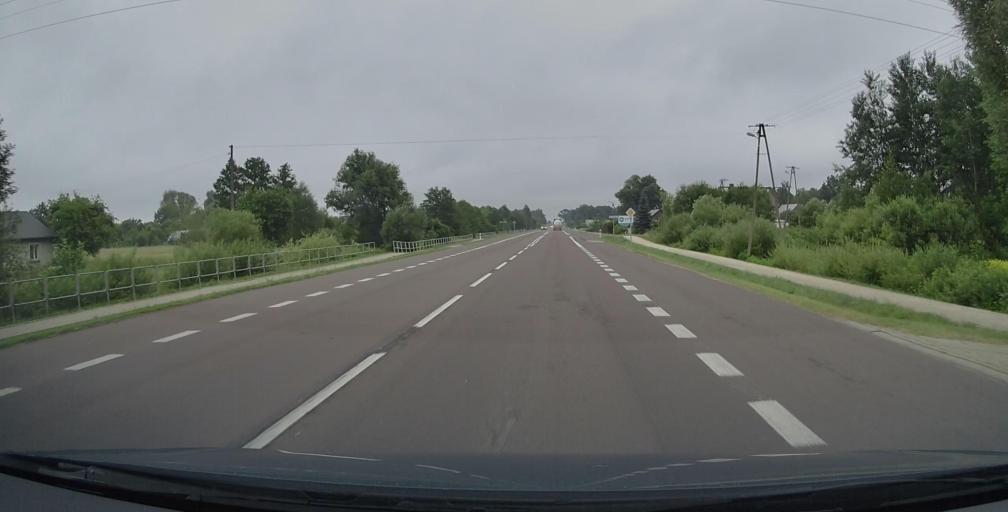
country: PL
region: Lublin Voivodeship
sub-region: Powiat bialski
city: Zalesie
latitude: 52.0369
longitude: 23.4588
